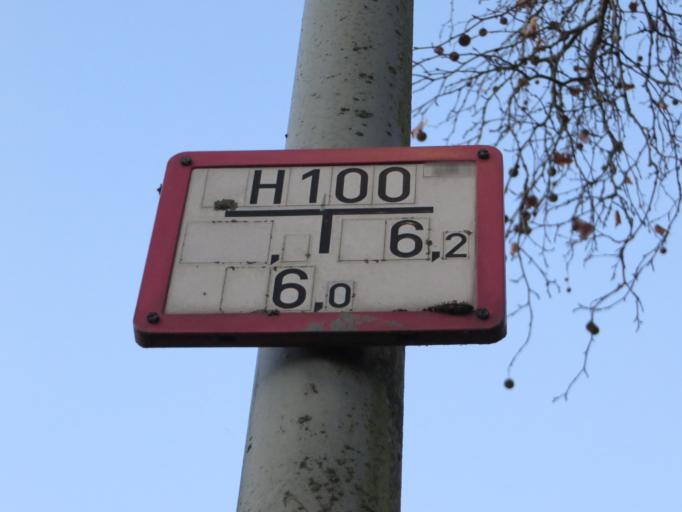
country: DE
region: North Rhine-Westphalia
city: Witten
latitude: 51.4361
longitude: 7.3418
